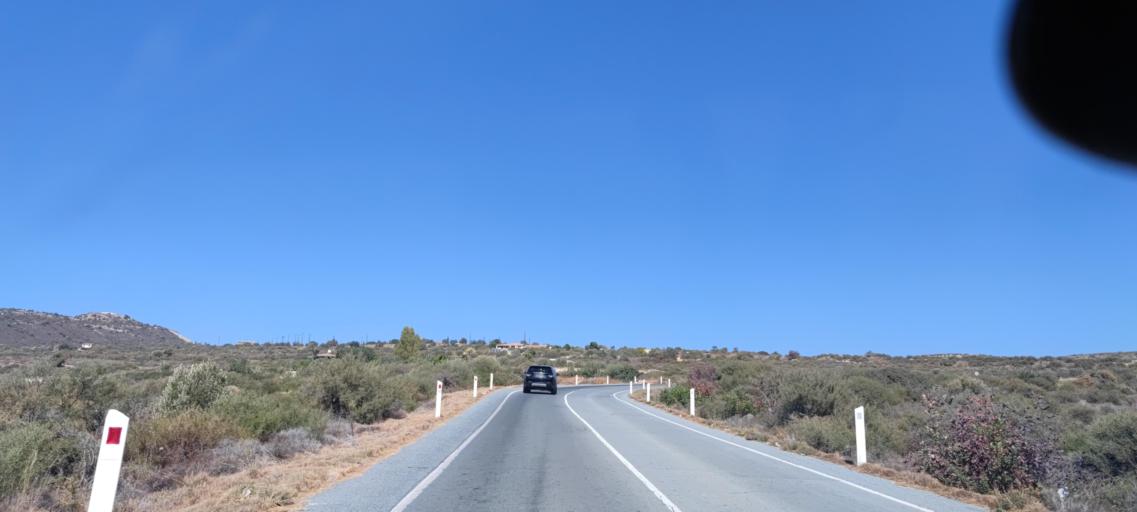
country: CY
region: Limassol
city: Mouttagiaka
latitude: 34.7400
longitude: 33.0624
